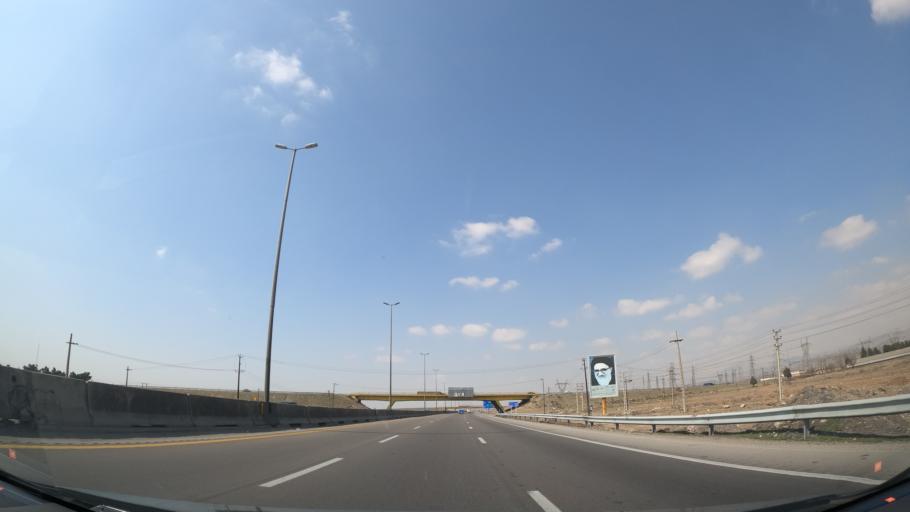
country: IR
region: Qazvin
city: Abyek
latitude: 36.0759
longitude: 50.4692
